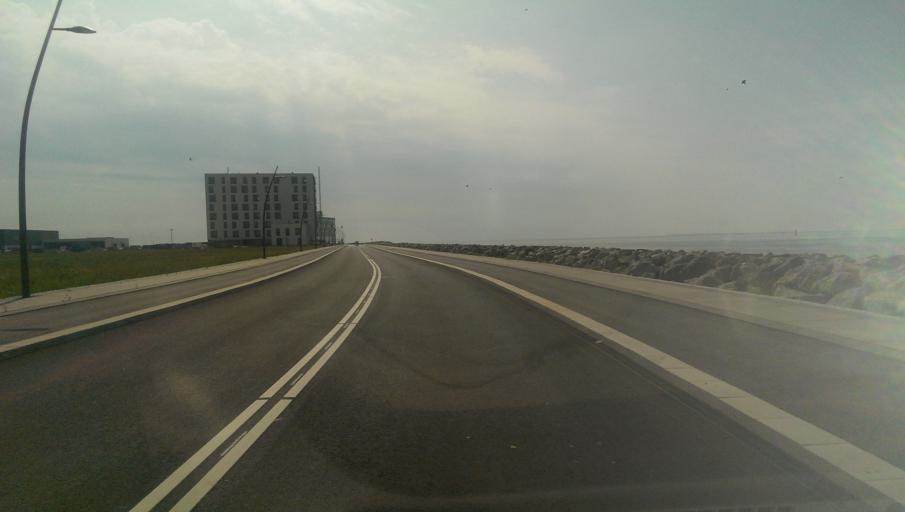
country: DK
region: South Denmark
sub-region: Esbjerg Kommune
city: Esbjerg
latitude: 55.4828
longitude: 8.4168
